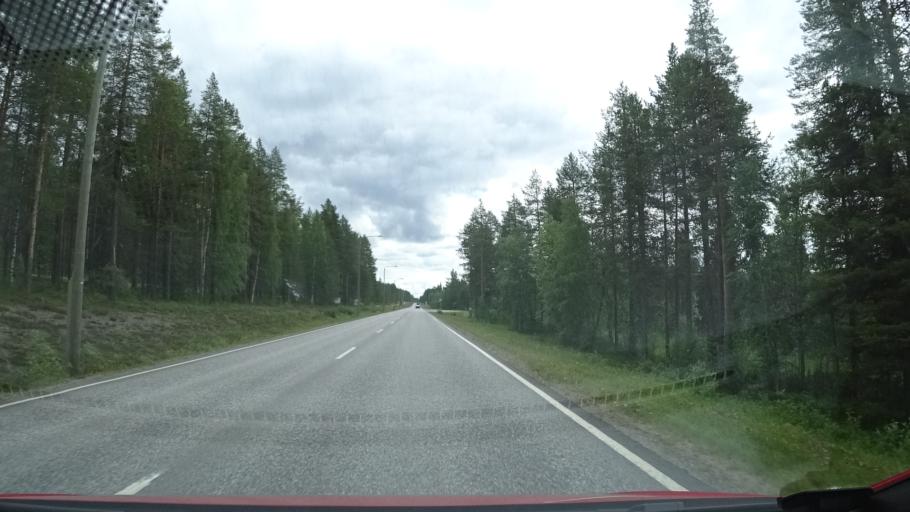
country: FI
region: Lapland
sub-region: Tunturi-Lappi
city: Kittilae
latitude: 67.7776
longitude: 24.8229
